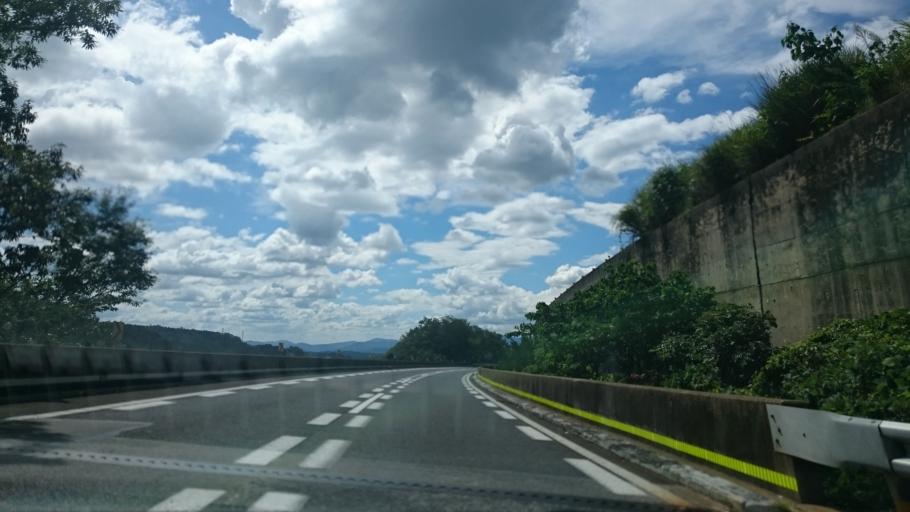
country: JP
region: Gifu
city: Nakatsugawa
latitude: 35.5087
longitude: 137.5489
